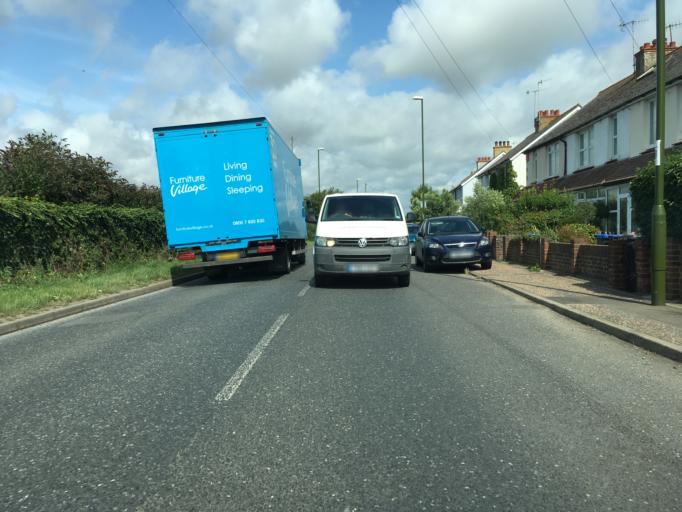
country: GB
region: England
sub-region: West Sussex
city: Shoreham-by-Sea
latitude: 50.8386
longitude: -0.2853
